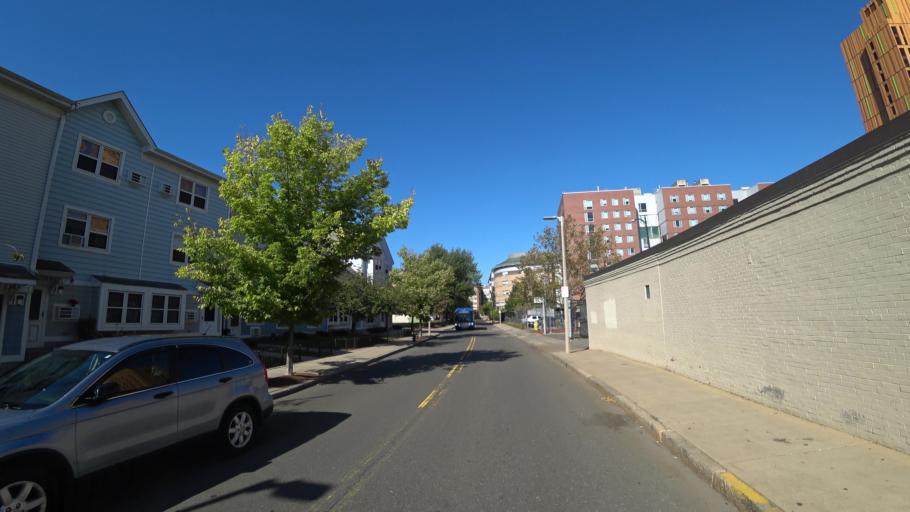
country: US
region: Massachusetts
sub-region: Norfolk County
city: Brookline
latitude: 42.3353
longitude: -71.0965
